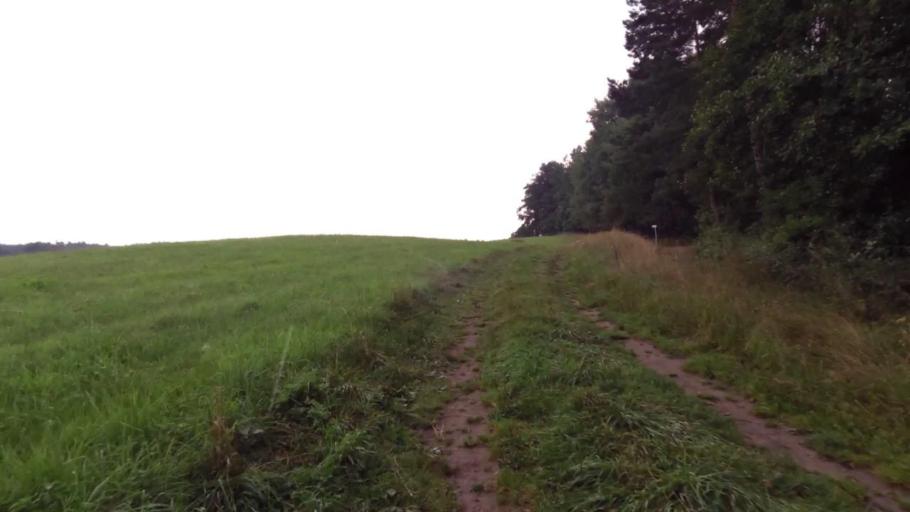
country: PL
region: West Pomeranian Voivodeship
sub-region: Powiat szczecinecki
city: Lubowo
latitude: 53.6085
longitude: 16.3840
